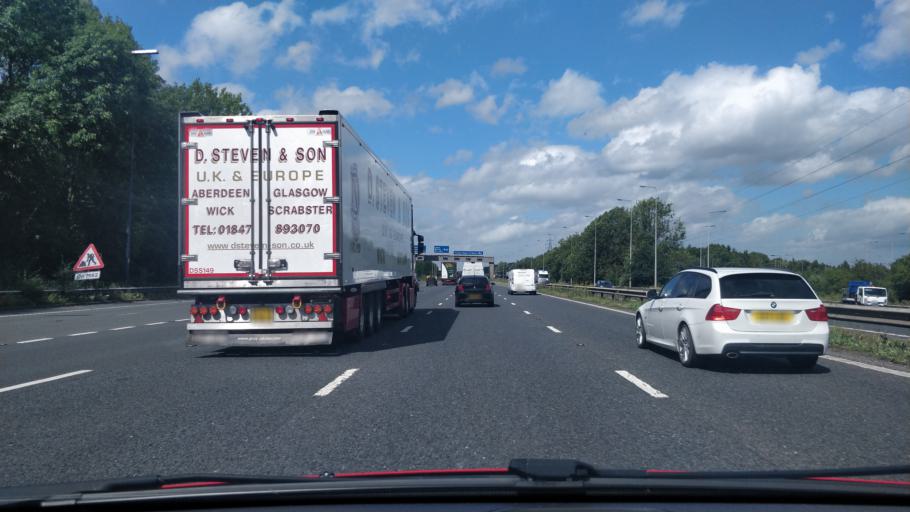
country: GB
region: England
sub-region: Warrington
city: Croft
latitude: 53.4204
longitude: -2.5477
